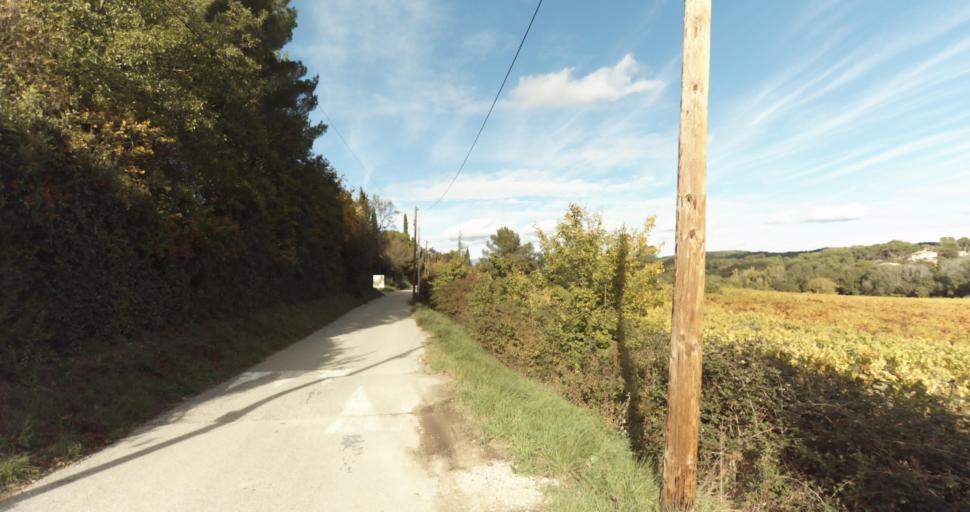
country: FR
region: Provence-Alpes-Cote d'Azur
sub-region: Departement des Bouches-du-Rhone
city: Venelles
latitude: 43.6058
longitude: 5.4857
